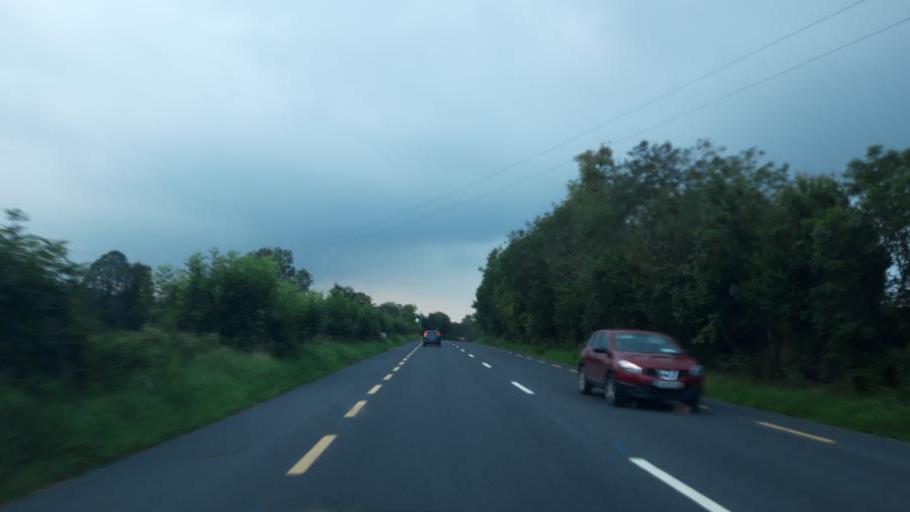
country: IE
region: Leinster
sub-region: Kilkenny
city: Thomastown
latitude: 52.5487
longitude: -7.1294
